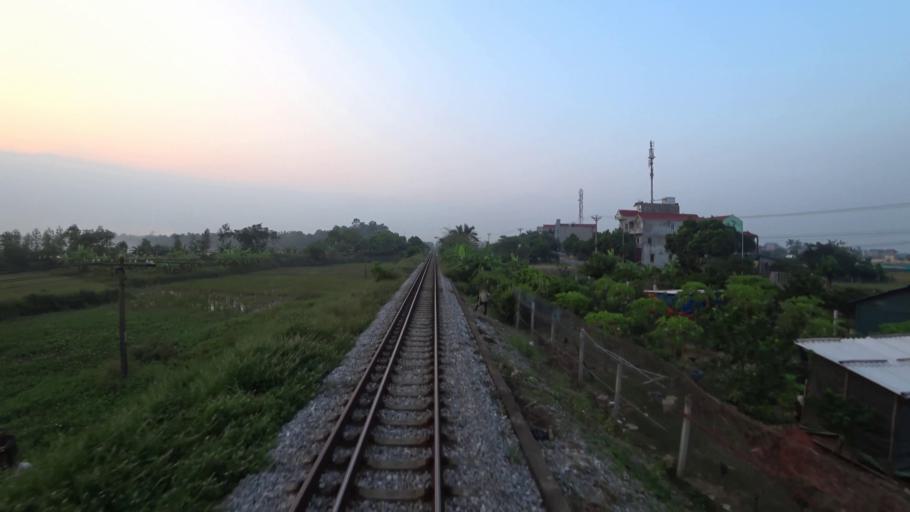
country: VN
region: Ha Noi
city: Dong Anh
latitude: 21.1312
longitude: 105.8752
